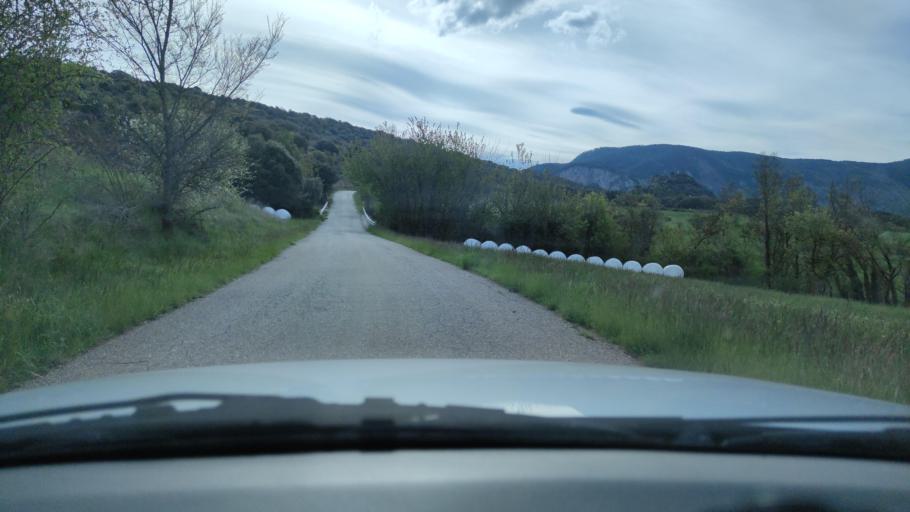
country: ES
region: Catalonia
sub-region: Provincia de Lleida
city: Coll de Nargo
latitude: 42.2339
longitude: 1.3928
